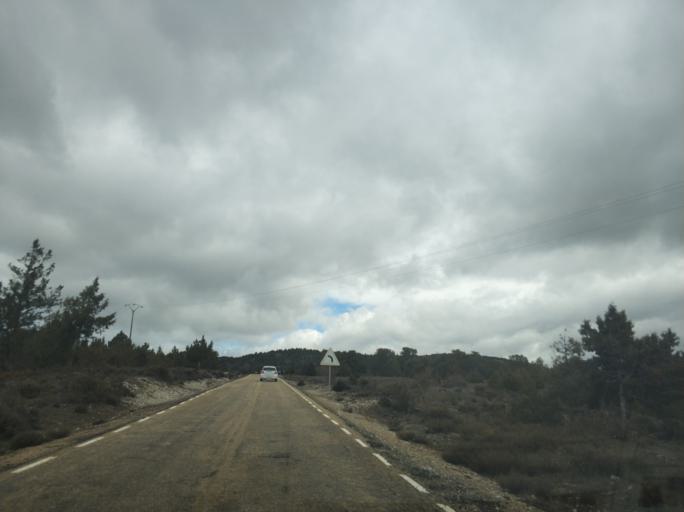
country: ES
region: Castille and Leon
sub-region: Provincia de Soria
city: Abejar
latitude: 41.7851
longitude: -2.7707
